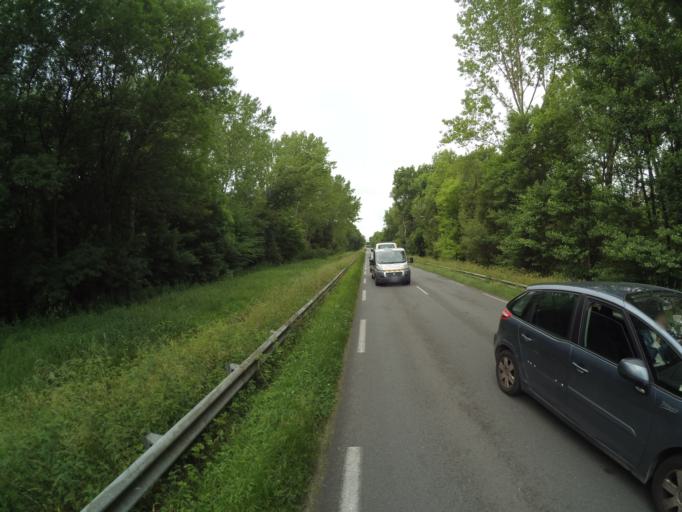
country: FR
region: Aquitaine
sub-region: Departement de la Gironde
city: Soussans
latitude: 45.0645
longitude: -0.7197
